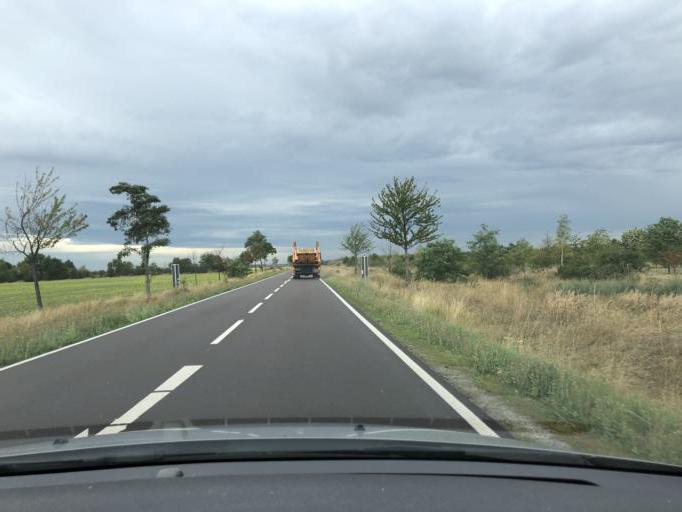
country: DE
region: Saxony-Anhalt
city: Gross Rosenburg
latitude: 51.8786
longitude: 11.8522
